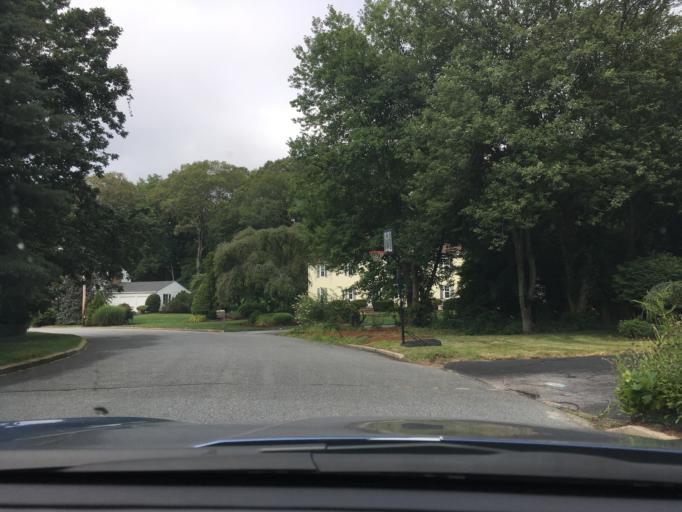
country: US
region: Rhode Island
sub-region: Kent County
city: East Greenwich
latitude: 41.6620
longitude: -71.4864
